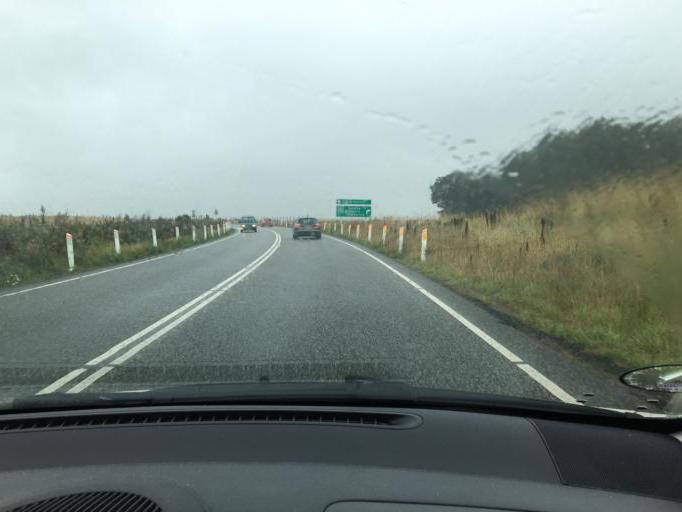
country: DK
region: South Denmark
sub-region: Vejle Kommune
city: Vejle
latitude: 55.6632
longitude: 9.5506
